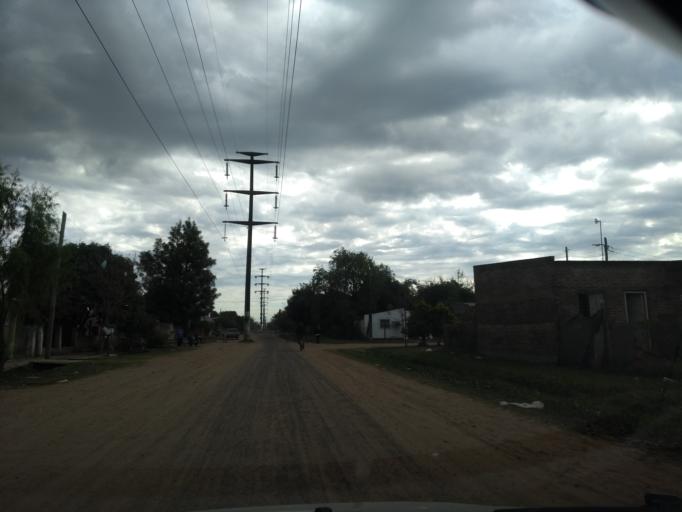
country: AR
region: Chaco
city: Barranqueras
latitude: -27.4722
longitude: -58.9197
